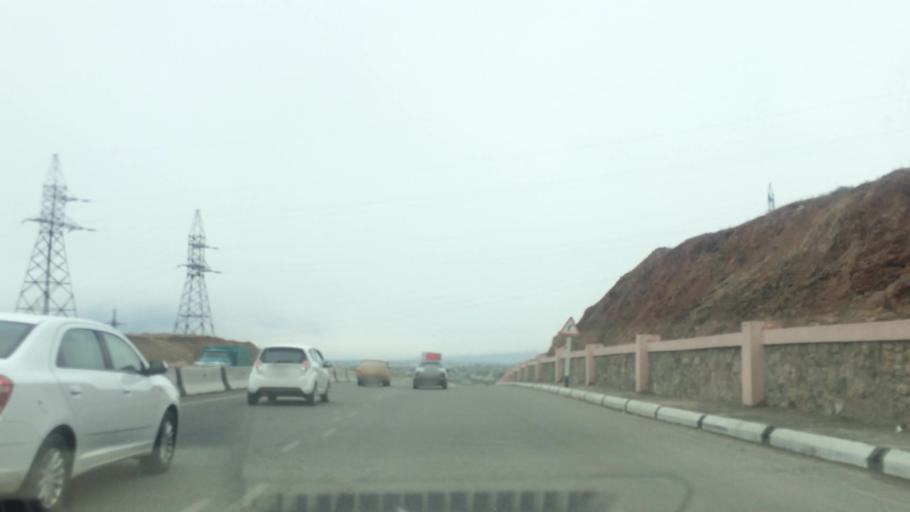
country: UZ
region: Samarqand
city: Jomboy
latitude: 39.6861
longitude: 67.0520
